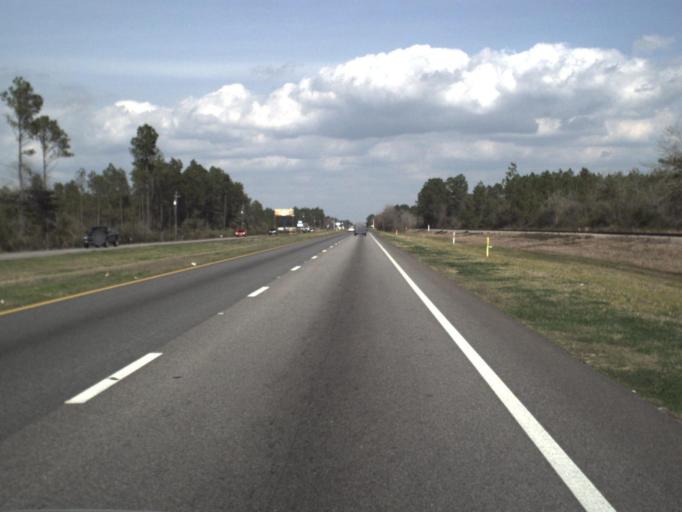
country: US
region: Florida
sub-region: Bay County
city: Hiland Park
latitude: 30.2349
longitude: -85.5766
